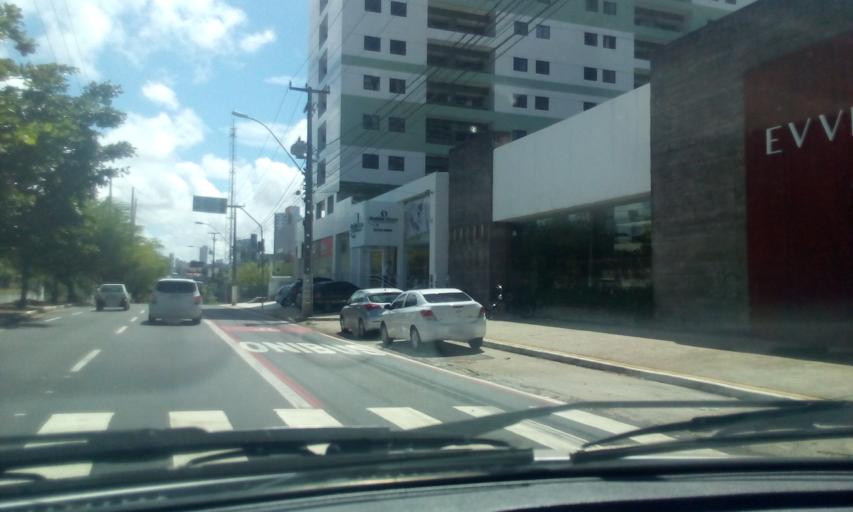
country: BR
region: Rio Grande do Norte
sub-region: Natal
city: Natal
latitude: -5.7935
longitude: -35.2034
